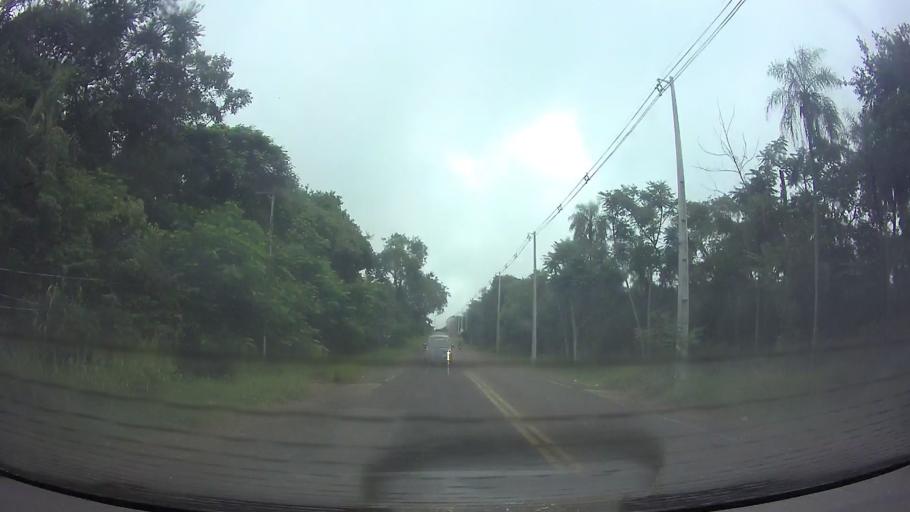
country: PY
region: Cordillera
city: Altos
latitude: -25.2764
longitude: -57.2609
